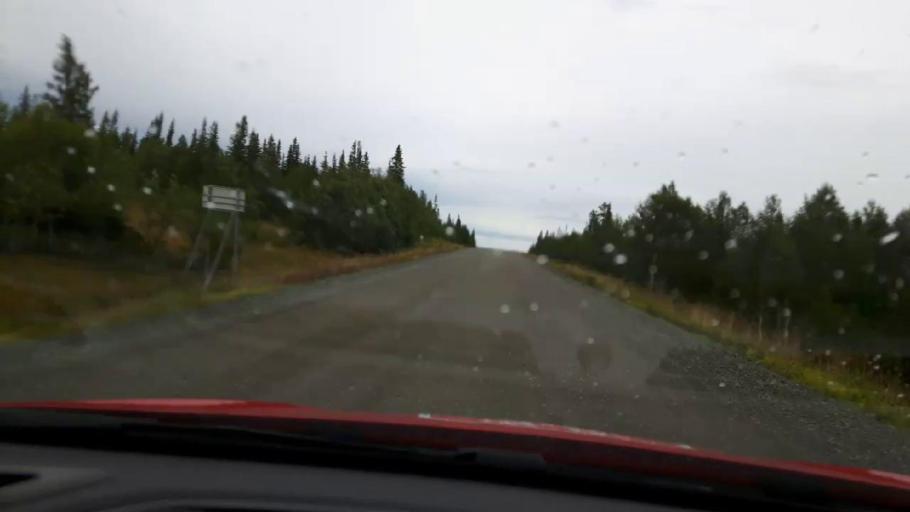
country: NO
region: Nord-Trondelag
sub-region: Meraker
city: Meraker
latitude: 63.5560
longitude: 12.3271
